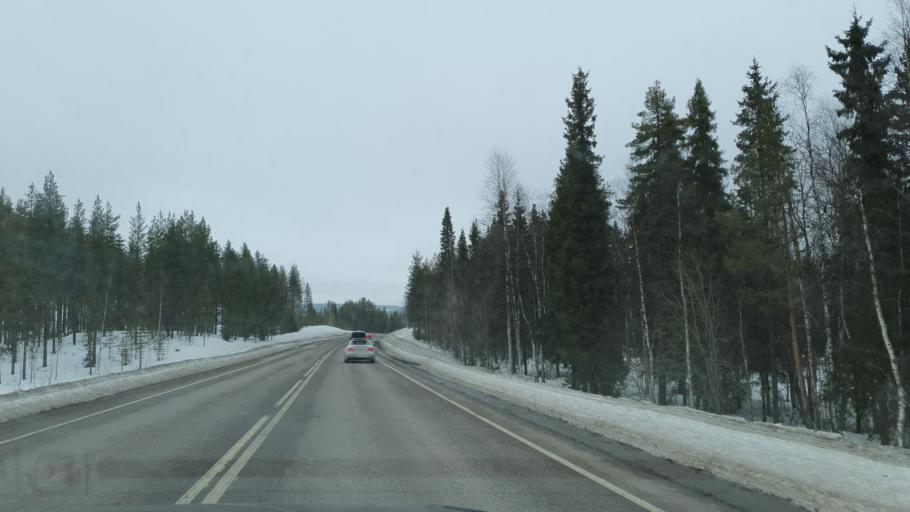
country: FI
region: Lapland
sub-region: Torniolaakso
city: Pello
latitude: 66.8660
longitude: 24.0504
